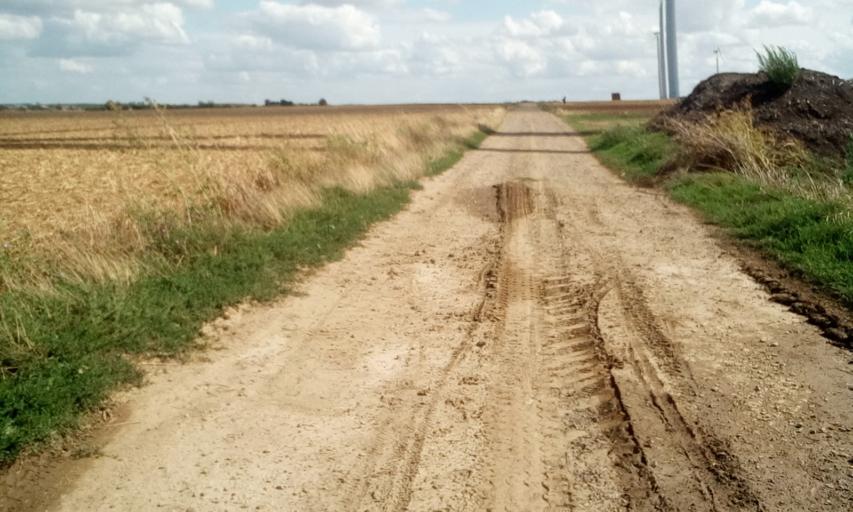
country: FR
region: Lower Normandy
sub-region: Departement du Calvados
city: Bellengreville
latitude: 49.1026
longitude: -0.2335
